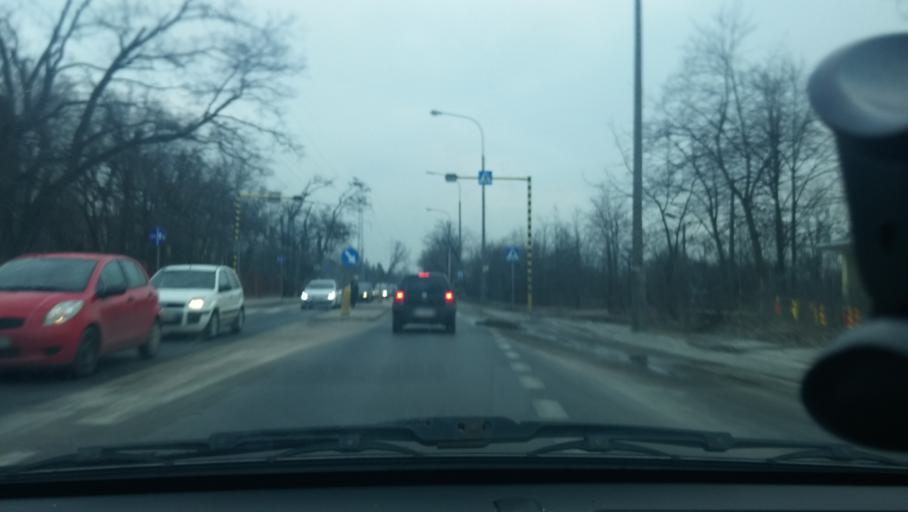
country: PL
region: Masovian Voivodeship
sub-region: Warszawa
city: Wawer
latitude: 52.2240
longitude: 21.1500
